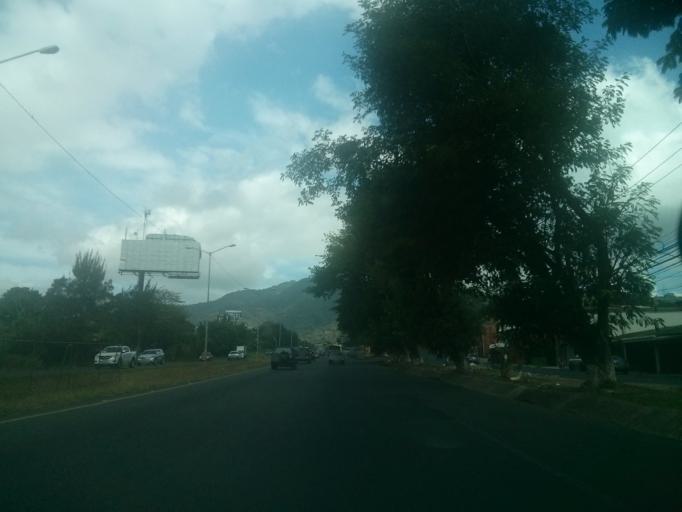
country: CR
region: Cartago
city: San Diego
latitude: 9.9056
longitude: -84.0119
